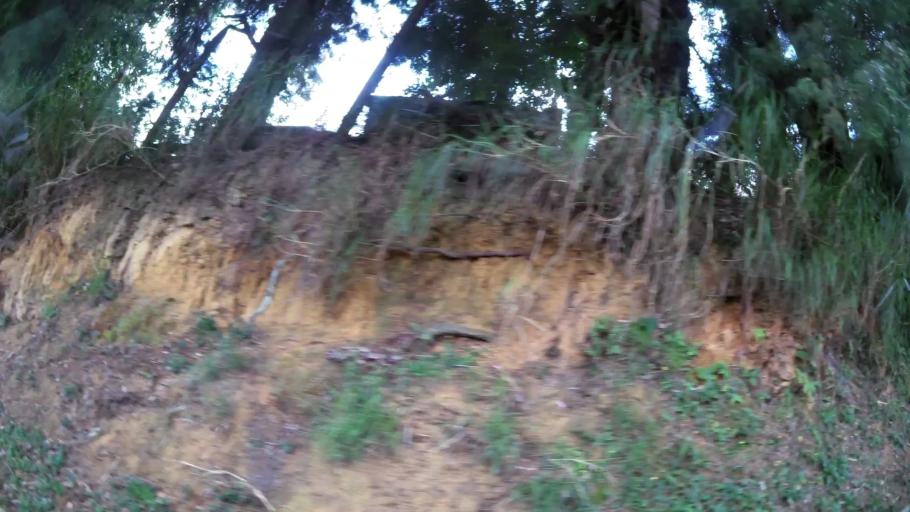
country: CO
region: Antioquia
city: La Estrella
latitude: 6.1728
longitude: -75.6585
